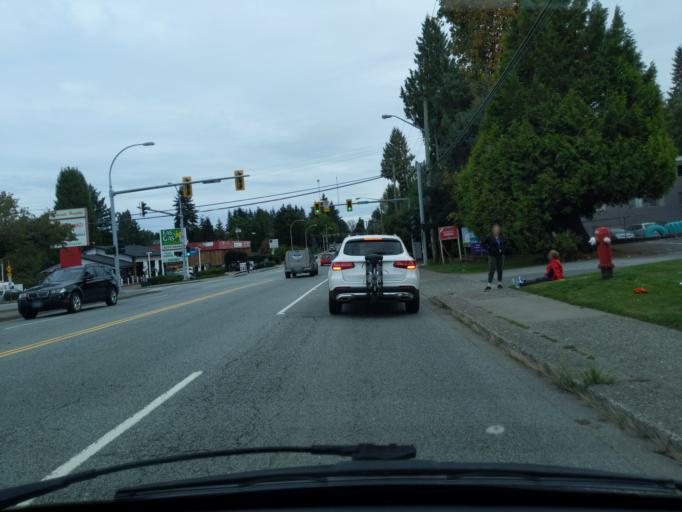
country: CA
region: British Columbia
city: Surrey
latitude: 49.1987
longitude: -122.8093
